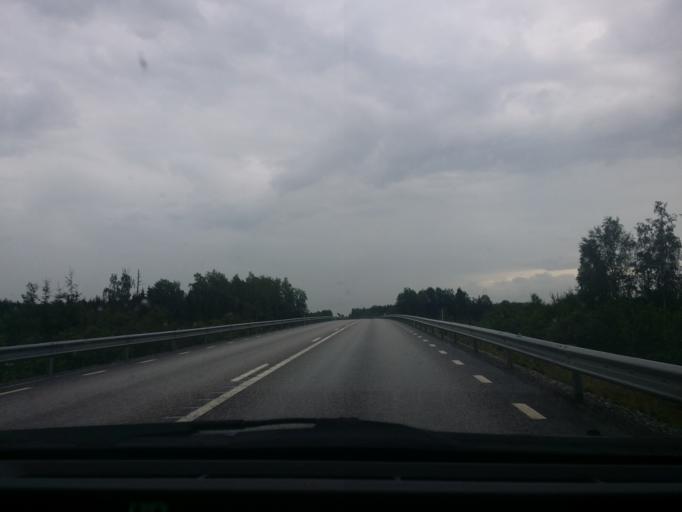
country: SE
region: OErebro
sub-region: Lindesbergs Kommun
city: Frovi
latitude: 59.4704
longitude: 15.4033
